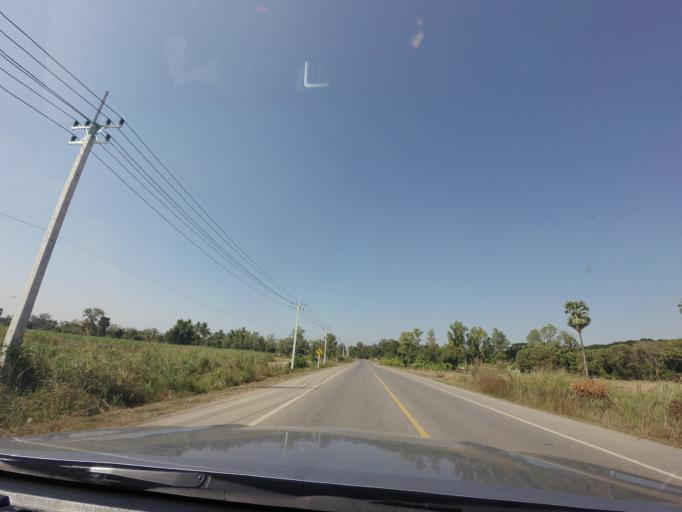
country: TH
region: Sukhothai
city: Sawankhalok
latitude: 17.3544
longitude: 99.8200
